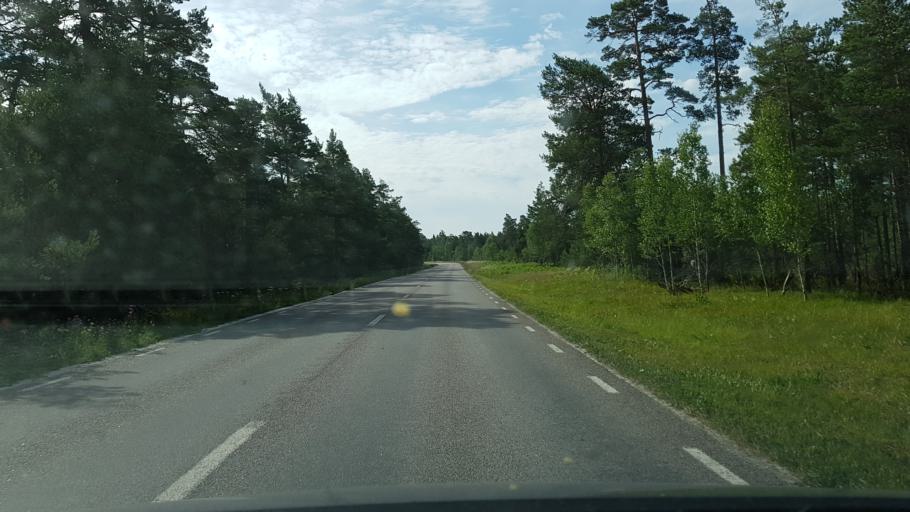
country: SE
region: Gotland
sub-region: Gotland
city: Hemse
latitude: 57.4563
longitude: 18.5774
